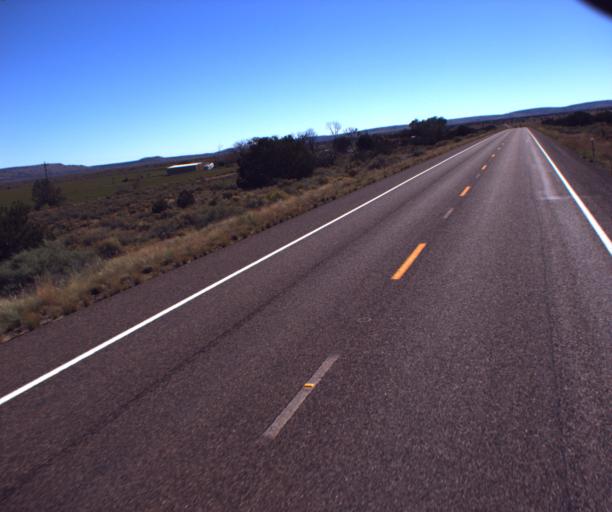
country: US
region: Arizona
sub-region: Apache County
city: Saint Johns
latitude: 34.6186
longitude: -109.6602
